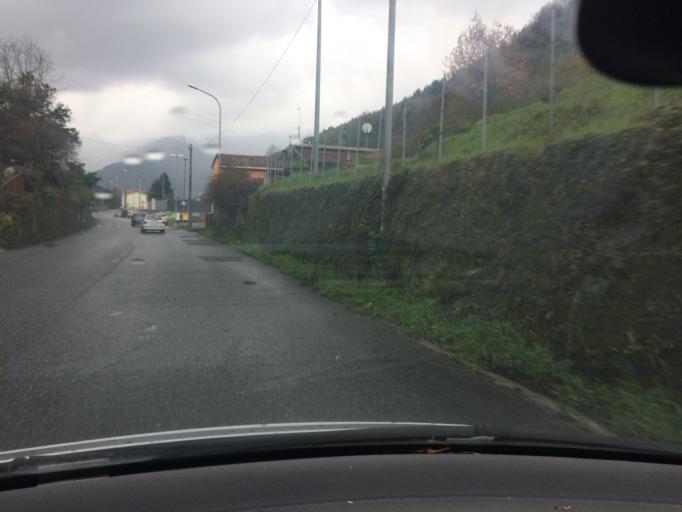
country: IT
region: Tuscany
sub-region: Provincia di Massa-Carrara
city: Massa
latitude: 44.0663
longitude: 10.1110
